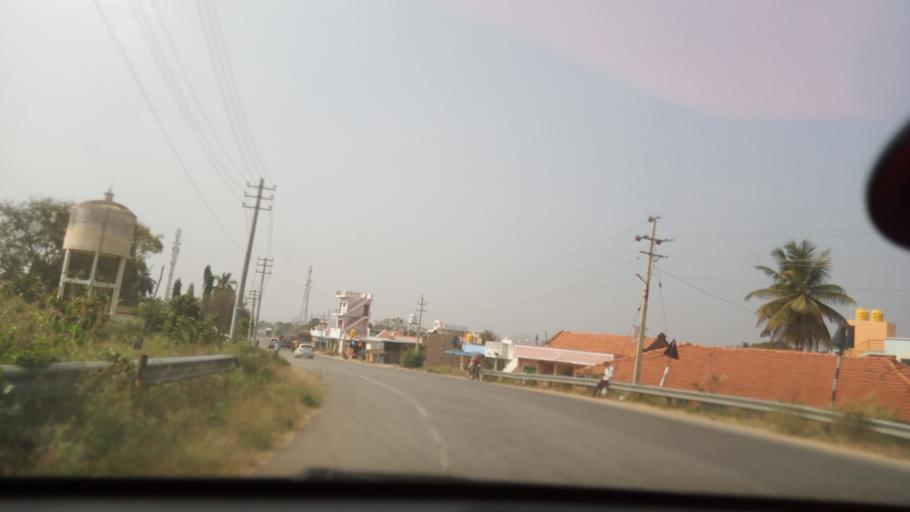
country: IN
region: Karnataka
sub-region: Chamrajnagar
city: Chamrajnagar
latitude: 11.9888
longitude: 76.8706
